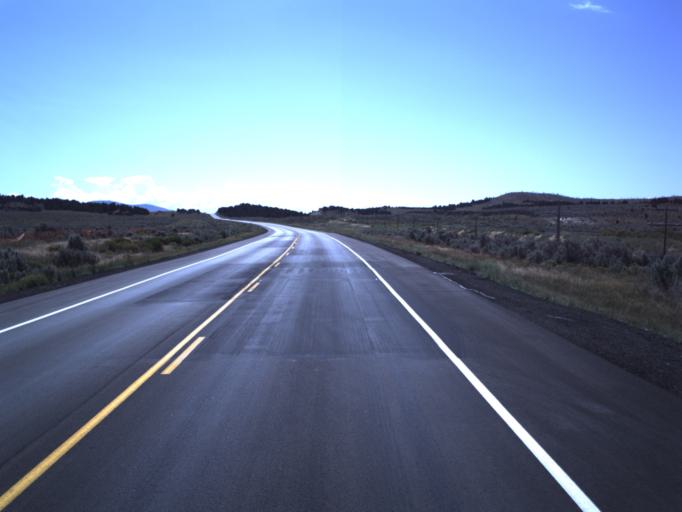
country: US
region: Utah
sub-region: Utah County
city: Genola
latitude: 39.9698
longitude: -112.2557
